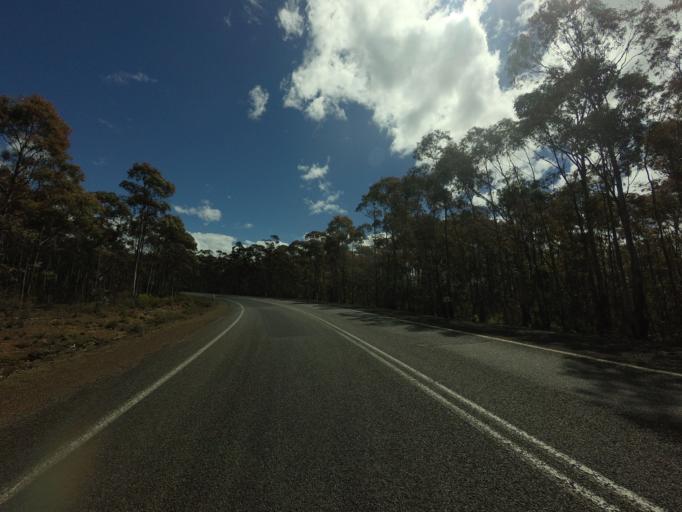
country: AU
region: Tasmania
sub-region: Break O'Day
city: St Helens
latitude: -42.0102
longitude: 147.9047
